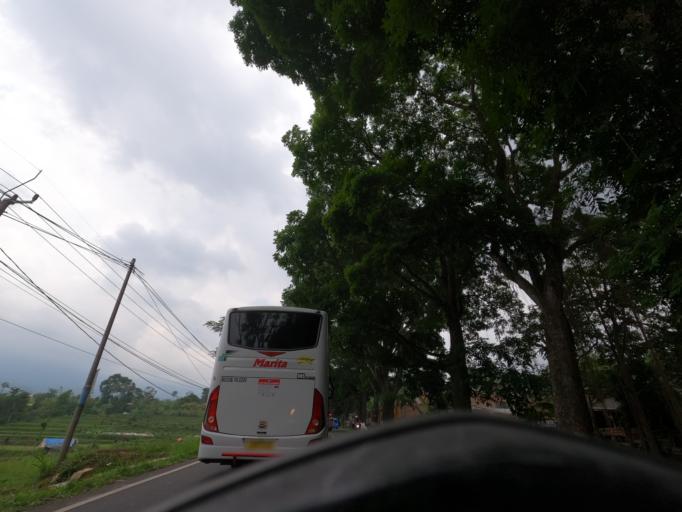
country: ID
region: West Java
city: Ciranjang-hilir
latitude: -6.7914
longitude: 107.0710
